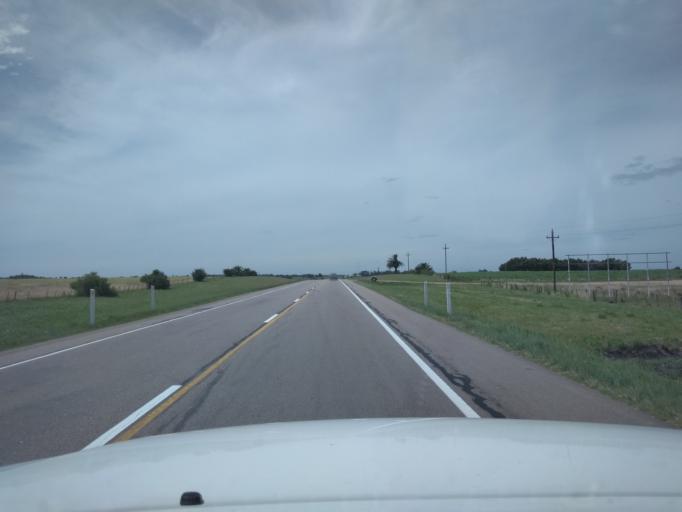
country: UY
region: Florida
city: Florida
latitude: -34.2278
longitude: -56.2116
